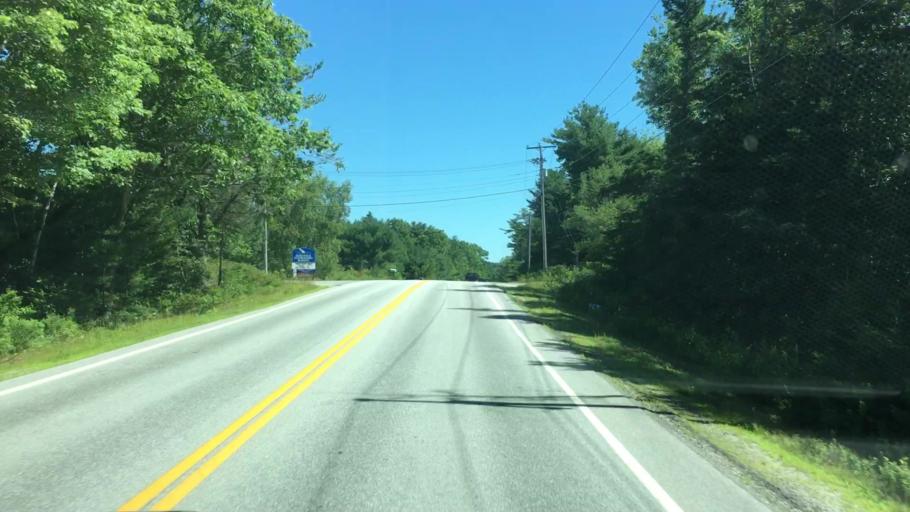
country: US
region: Maine
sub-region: Hancock County
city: Sedgwick
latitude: 44.3588
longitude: -68.6641
